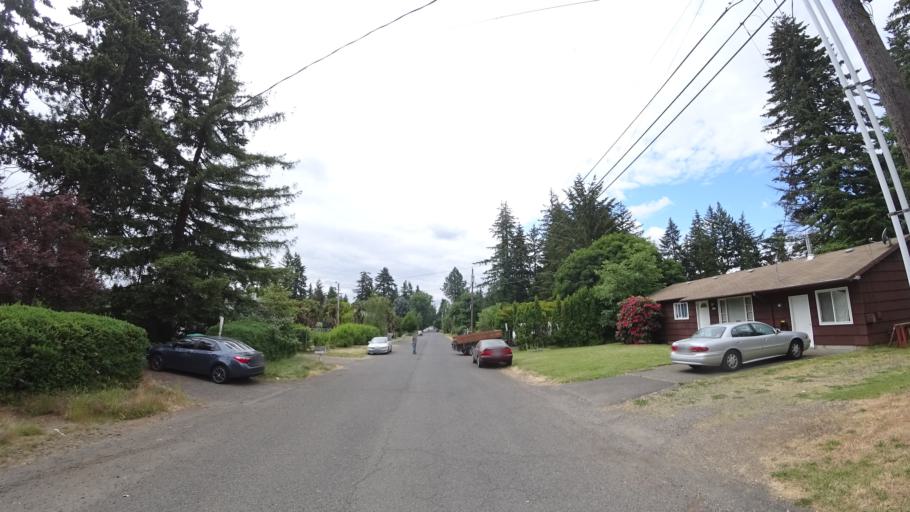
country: US
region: Oregon
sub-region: Multnomah County
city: Lents
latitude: 45.5031
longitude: -122.5262
